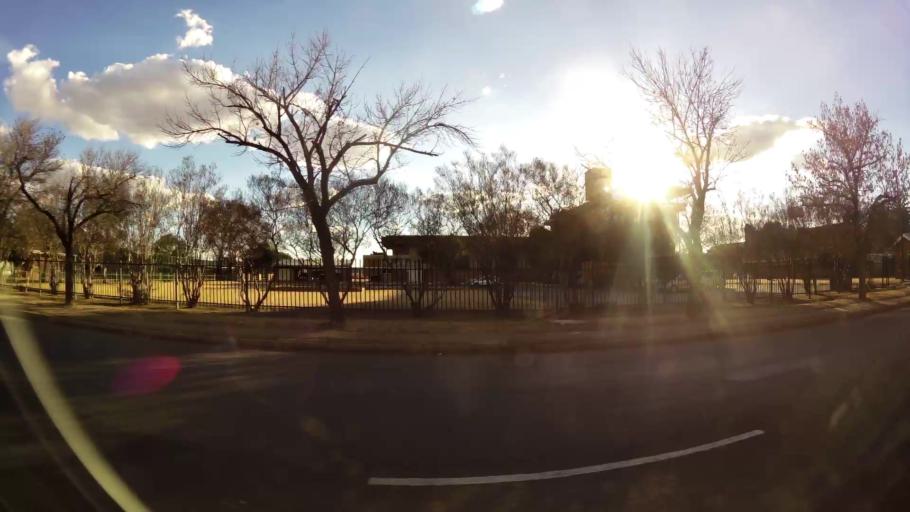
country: ZA
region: North-West
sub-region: Dr Kenneth Kaunda District Municipality
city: Potchefstroom
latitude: -26.7311
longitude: 27.0841
